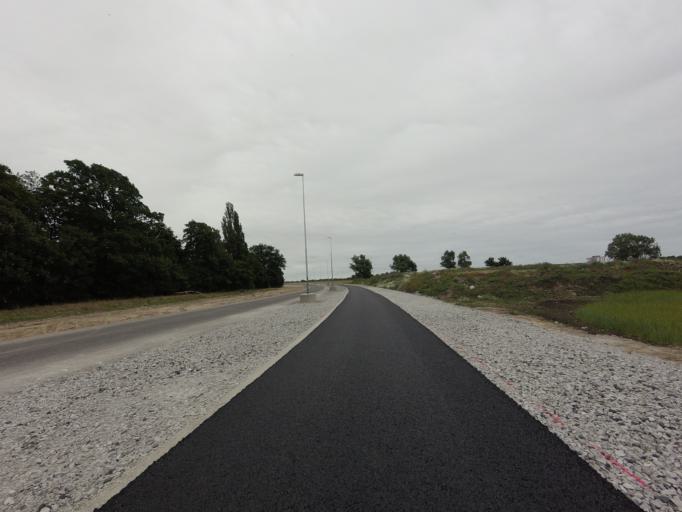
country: SE
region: Skane
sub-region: Malmo
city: Bunkeflostrand
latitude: 55.5635
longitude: 12.9440
